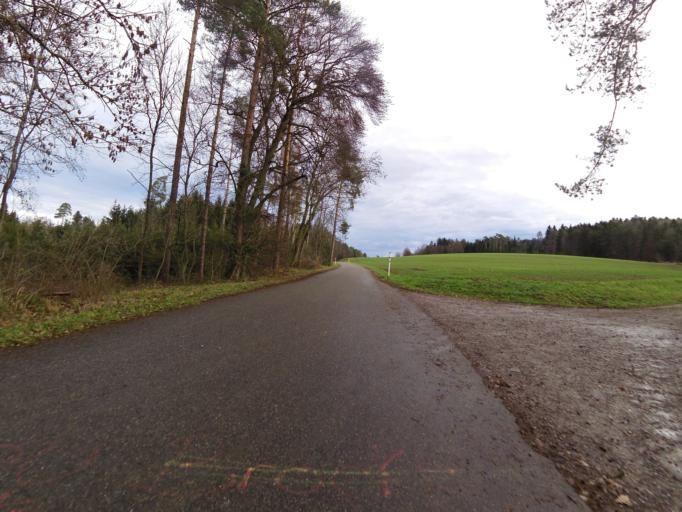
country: CH
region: Thurgau
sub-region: Frauenfeld District
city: Frauenfeld
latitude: 47.5505
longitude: 8.9248
